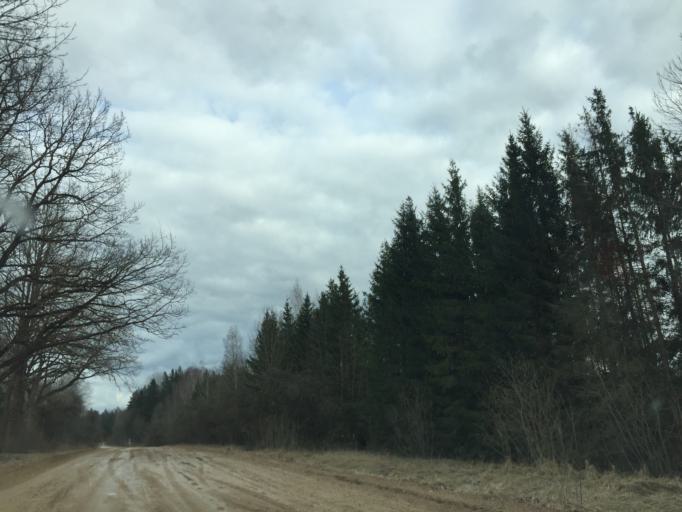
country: LV
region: Lielvarde
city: Lielvarde
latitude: 56.5265
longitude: 24.7747
